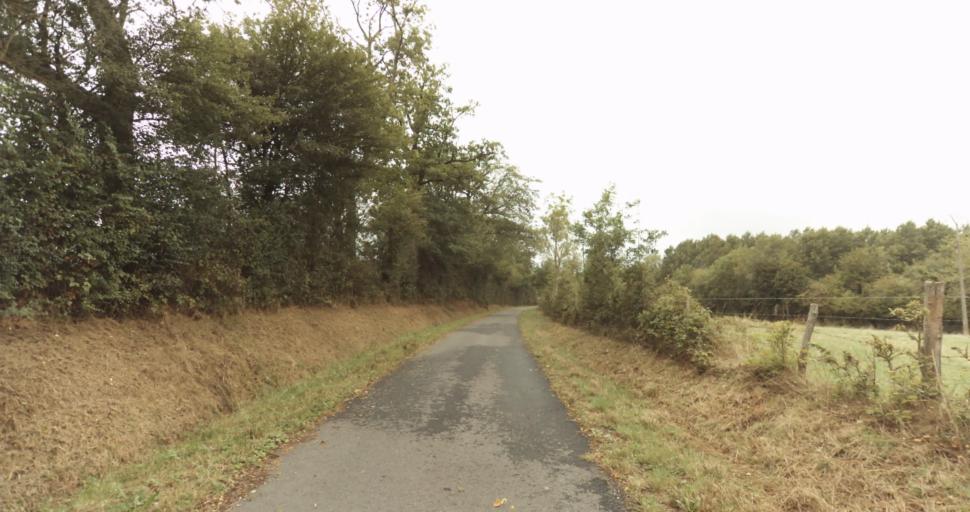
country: FR
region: Lower Normandy
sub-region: Departement de l'Orne
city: Sainte-Gauburge-Sainte-Colombe
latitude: 48.7137
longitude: 0.4441
